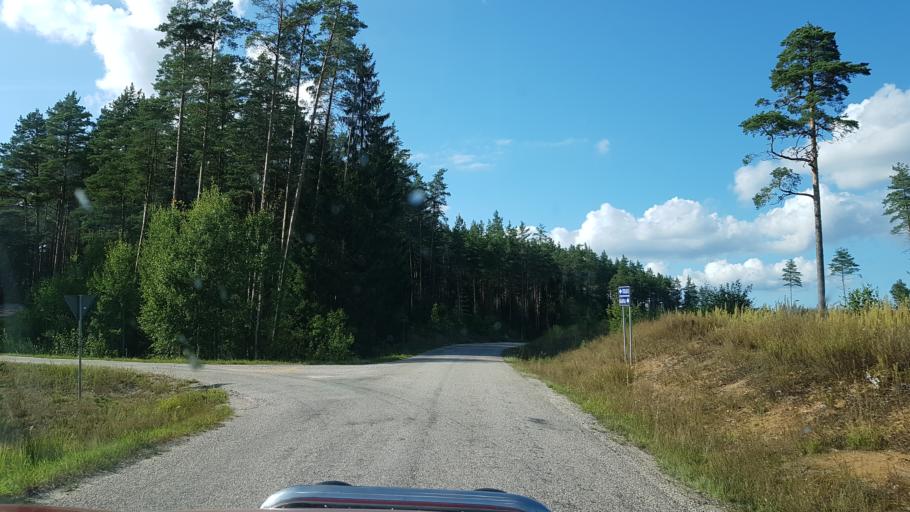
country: EE
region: Vorumaa
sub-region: Voru linn
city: Voru
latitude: 57.8870
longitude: 27.1066
